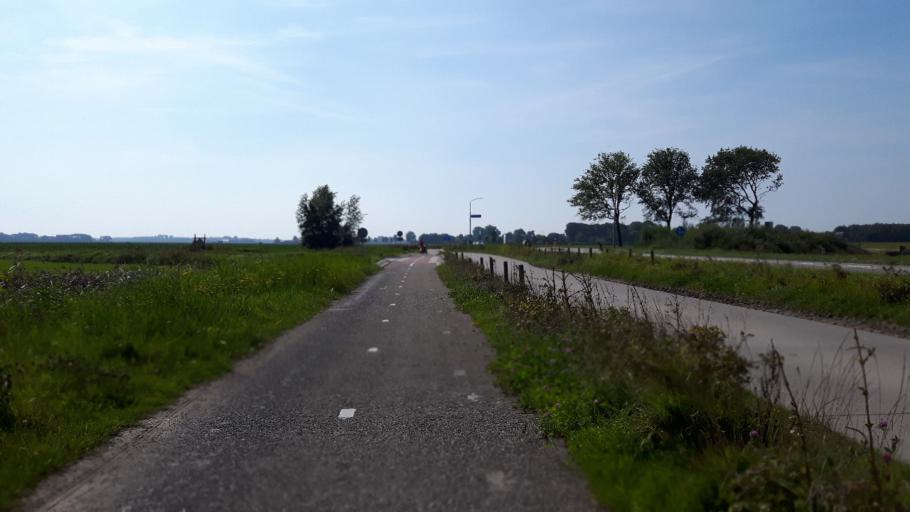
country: NL
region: Friesland
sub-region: Gemeente Ferwerderadiel
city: Hallum
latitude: 53.2970
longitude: 5.7742
